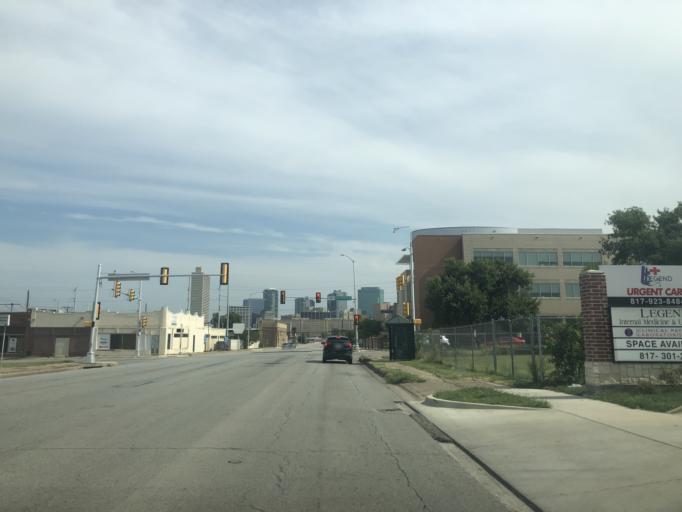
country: US
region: Texas
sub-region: Tarrant County
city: Fort Worth
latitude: 32.7378
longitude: -97.3318
